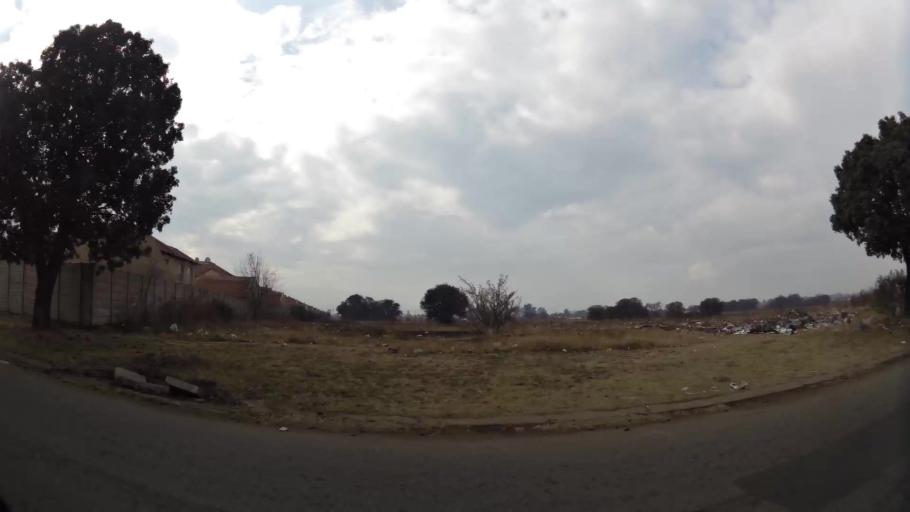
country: ZA
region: Gauteng
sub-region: Sedibeng District Municipality
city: Vanderbijlpark
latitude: -26.6802
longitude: 27.8390
